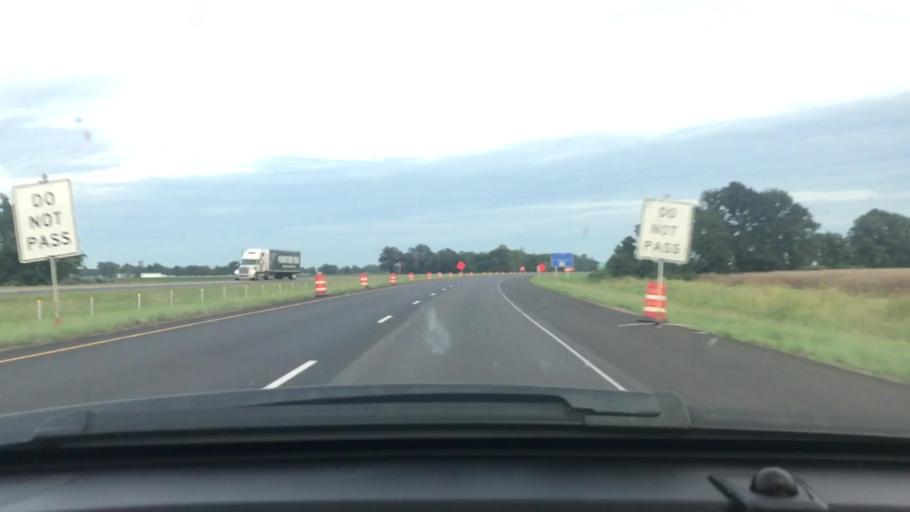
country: US
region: Arkansas
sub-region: Poinsett County
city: Trumann
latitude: 35.6452
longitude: -90.5151
